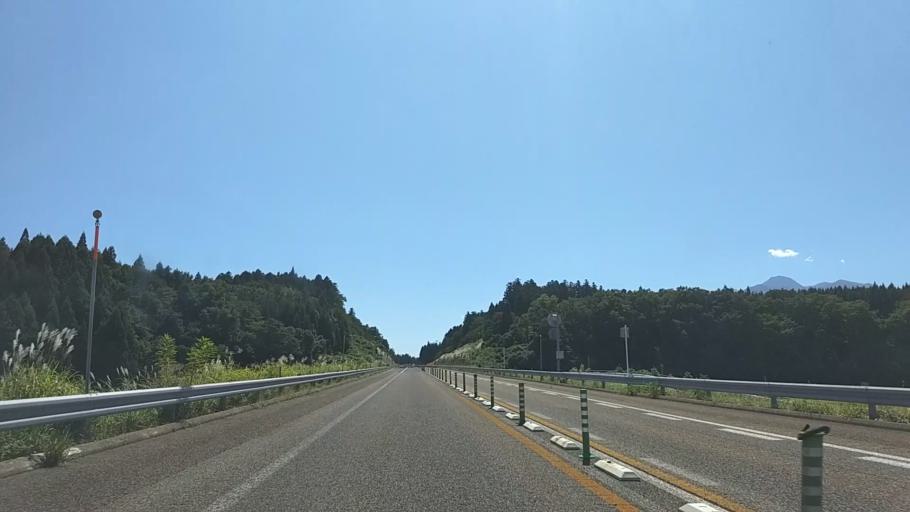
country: JP
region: Niigata
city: Arai
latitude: 37.0026
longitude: 138.2079
